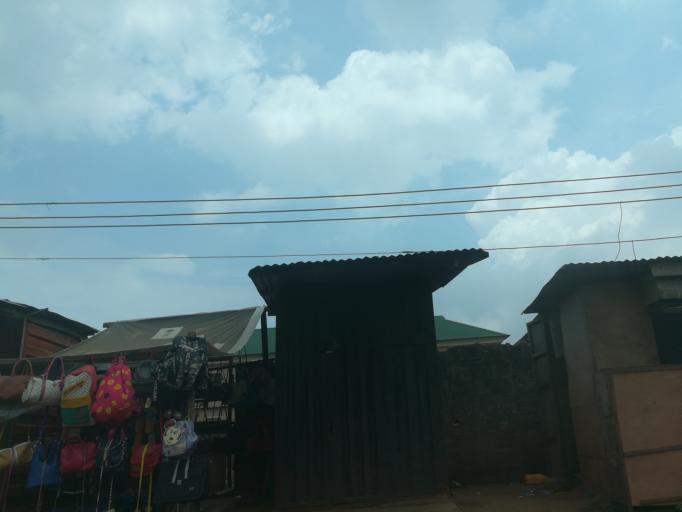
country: NG
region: Lagos
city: Ikorodu
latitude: 6.6211
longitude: 3.5204
